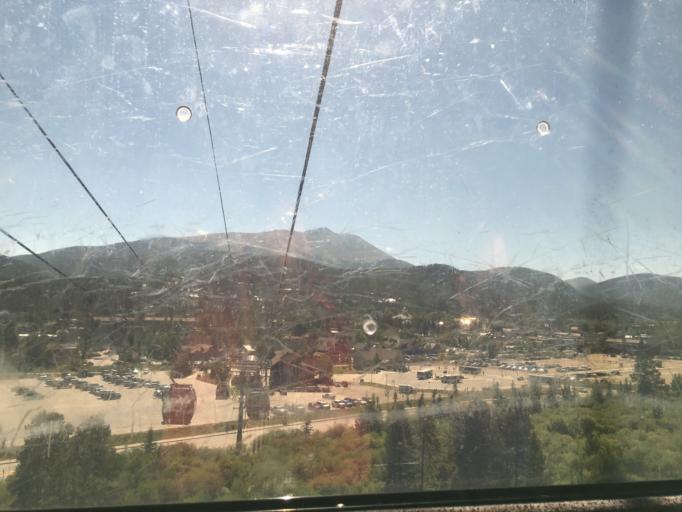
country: US
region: Colorado
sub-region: Summit County
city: Breckenridge
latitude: 39.4864
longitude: -106.0499
